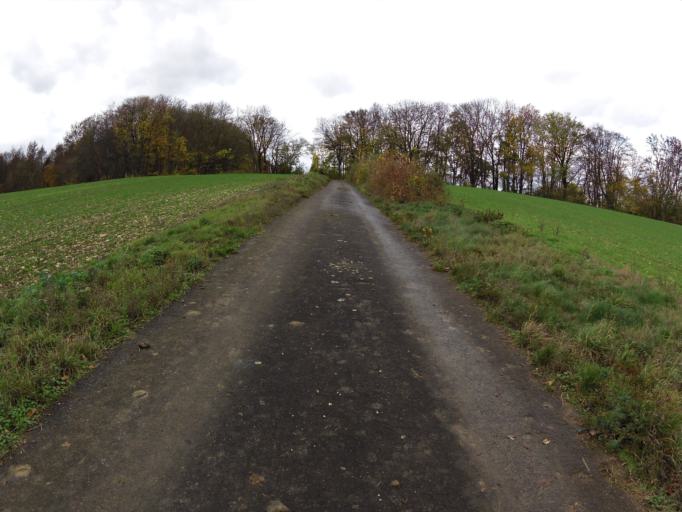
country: DE
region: Hesse
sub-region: Regierungsbezirk Kassel
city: Herleshausen
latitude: 51.0450
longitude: 10.1275
